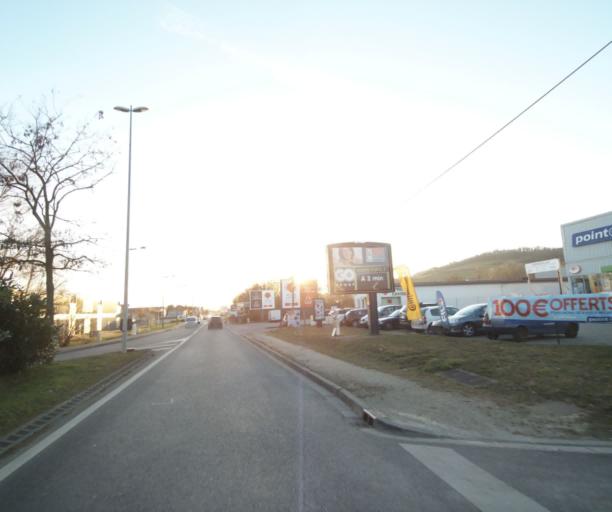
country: FR
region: Lorraine
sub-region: Departement de Meurthe-et-Moselle
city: Pulnoy
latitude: 48.7125
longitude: 6.2475
